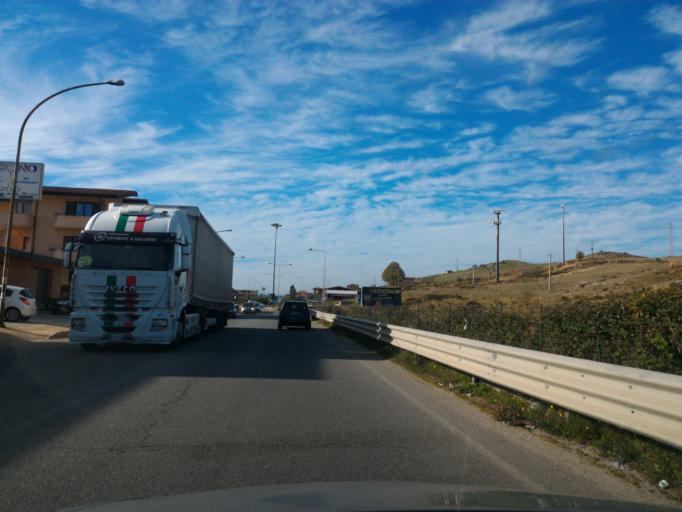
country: IT
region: Calabria
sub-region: Provincia di Catanzaro
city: Cropani Marina
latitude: 38.9224
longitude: 16.8050
